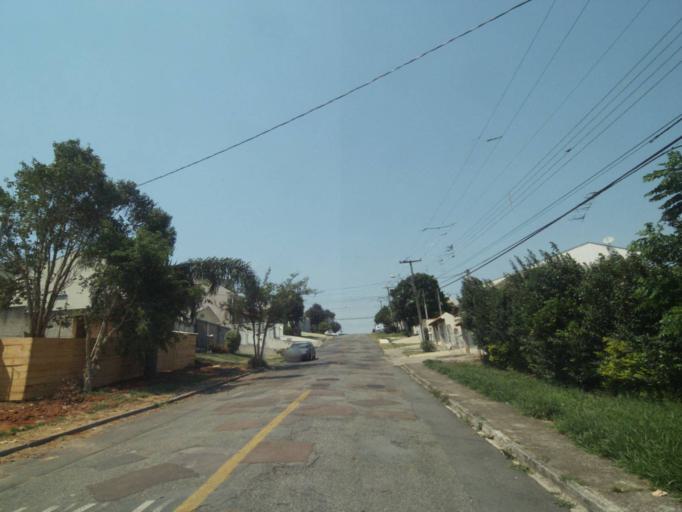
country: BR
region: Parana
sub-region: Sao Jose Dos Pinhais
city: Sao Jose dos Pinhais
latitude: -25.5063
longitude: -49.2665
